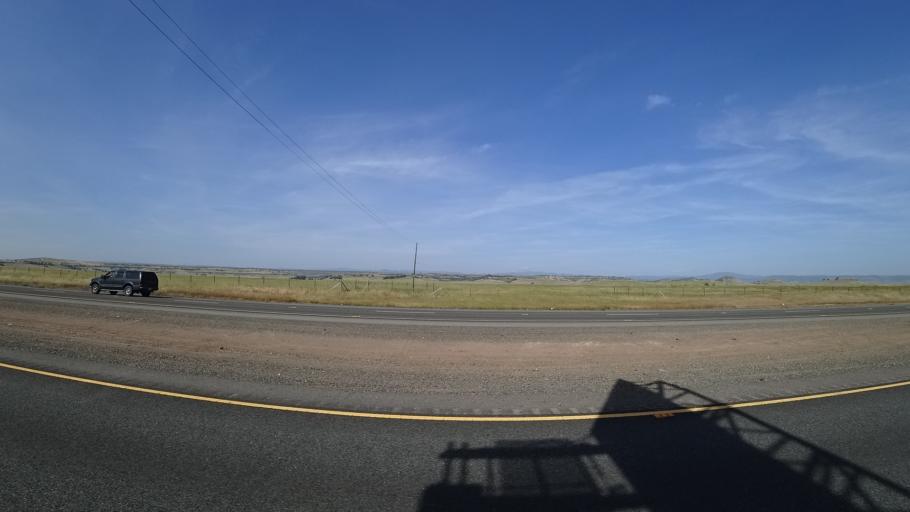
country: US
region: California
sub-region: Butte County
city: Durham
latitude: 39.6477
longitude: -121.7224
